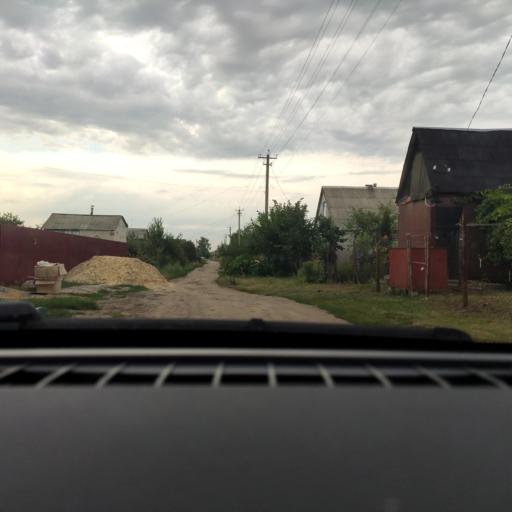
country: RU
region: Voronezj
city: Maslovka
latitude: 51.5204
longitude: 39.2325
